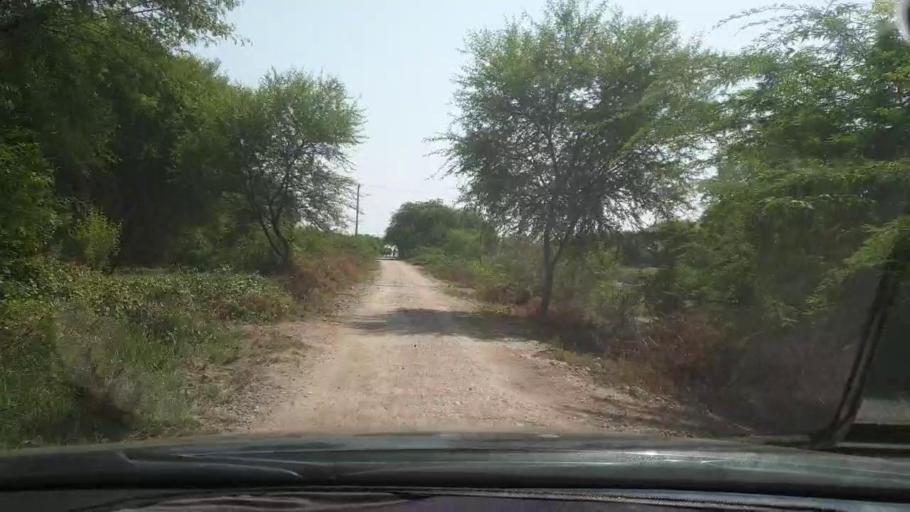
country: PK
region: Sindh
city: Naukot
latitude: 24.8125
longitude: 69.2442
